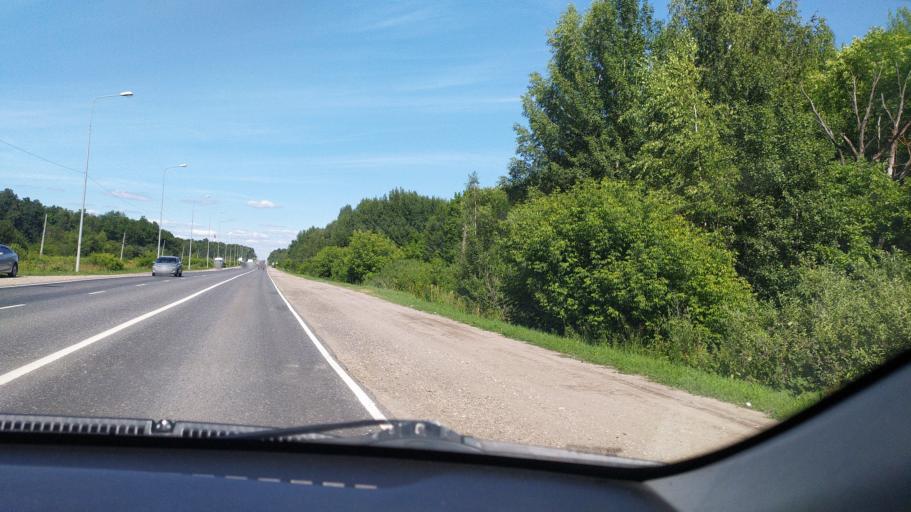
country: RU
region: Chuvashia
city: Novyye Lapsary
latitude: 56.0852
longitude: 47.2389
